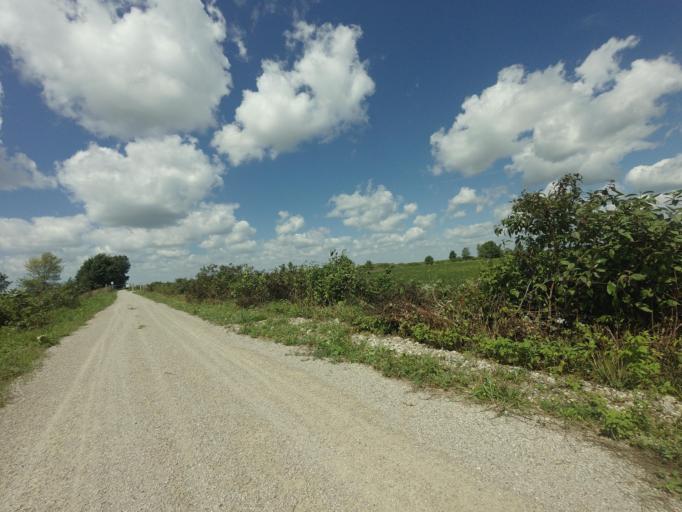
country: CA
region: Ontario
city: North Perth
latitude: 43.5711
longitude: -81.0357
